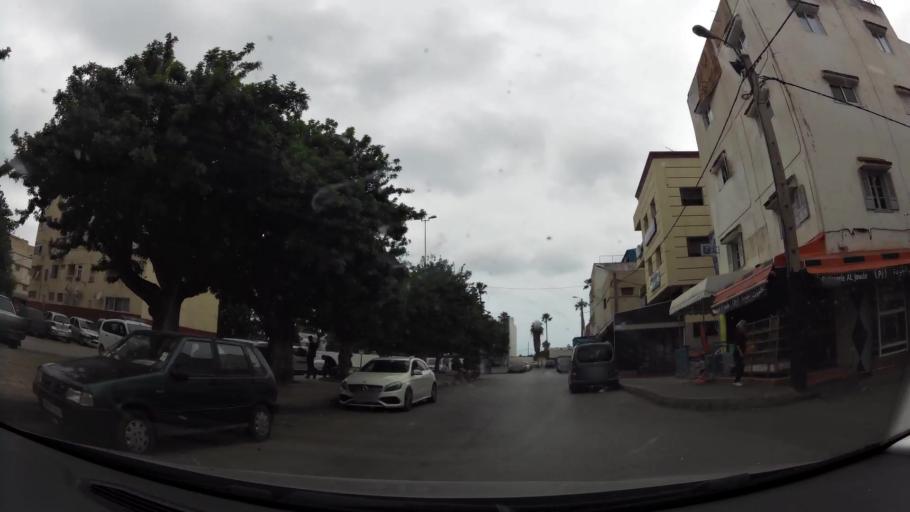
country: MA
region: Rabat-Sale-Zemmour-Zaer
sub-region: Rabat
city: Rabat
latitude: 33.9841
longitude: -6.8233
